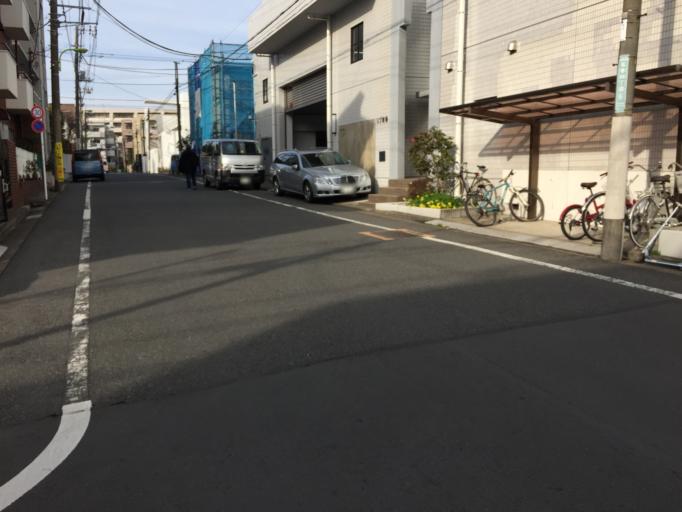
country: JP
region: Tokyo
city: Tokyo
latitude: 35.6342
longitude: 139.6419
